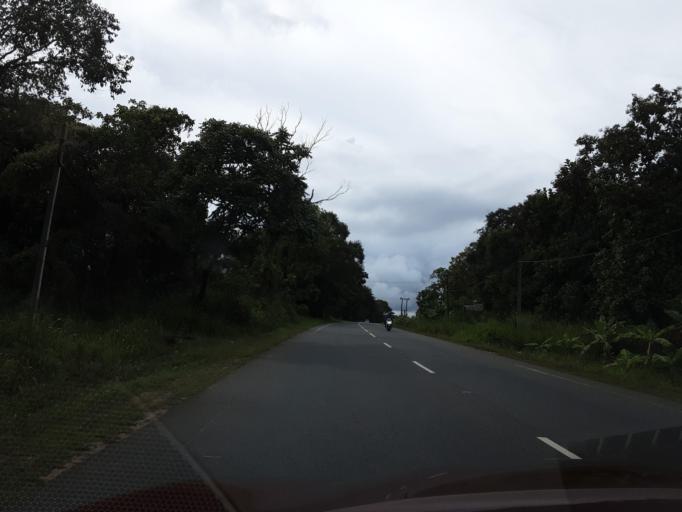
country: LK
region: Uva
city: Badulla
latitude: 7.3879
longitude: 81.1442
